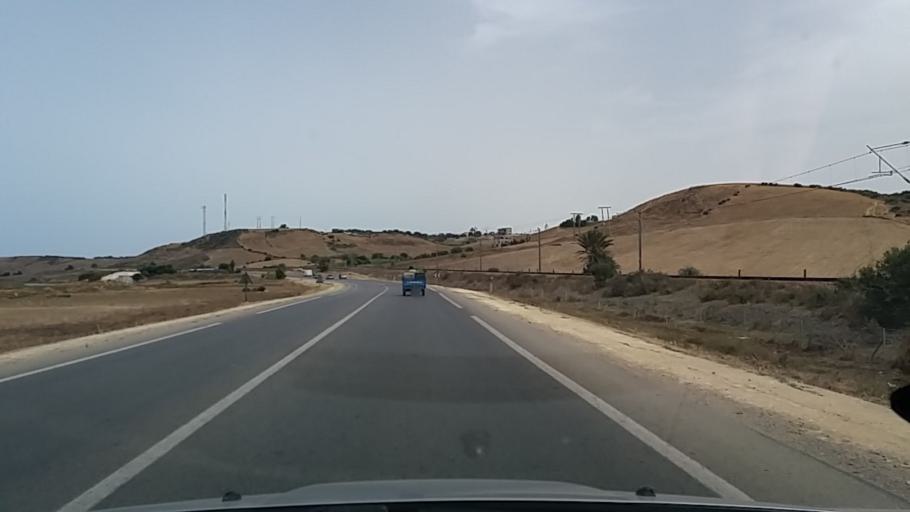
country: MA
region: Tanger-Tetouan
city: Asilah
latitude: 35.5101
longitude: -5.9992
